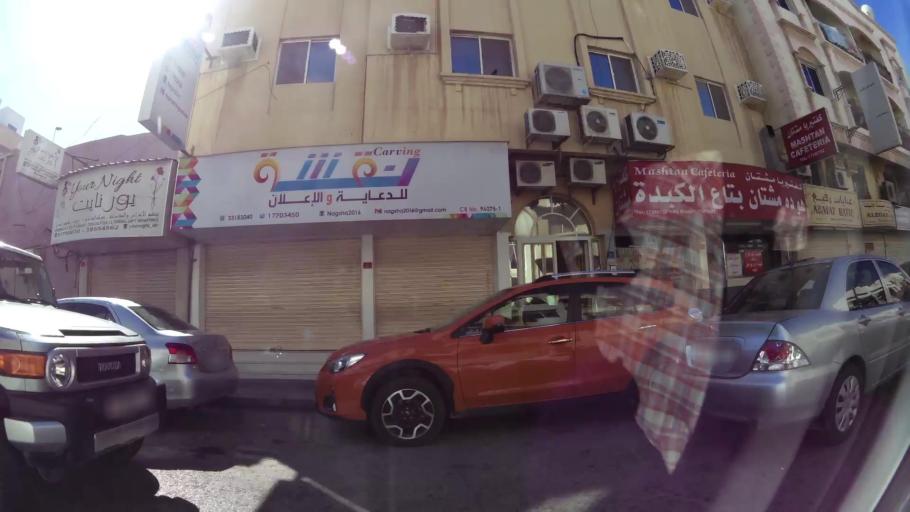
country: BH
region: Muharraq
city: Al Muharraq
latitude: 26.2582
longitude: 50.6177
